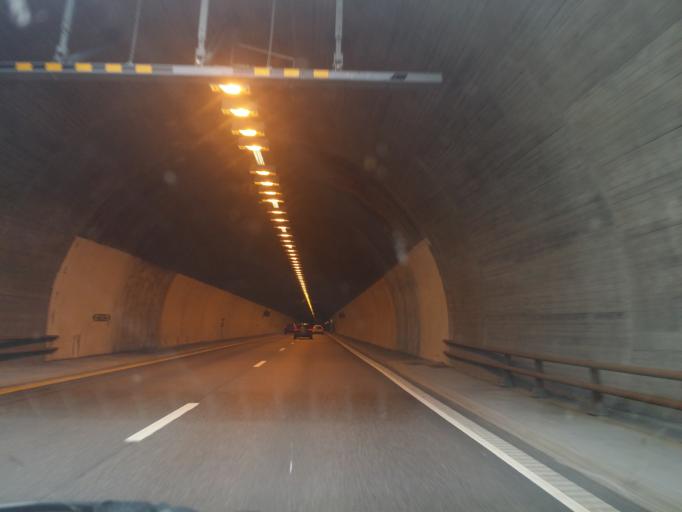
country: NO
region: Akershus
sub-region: Eidsvoll
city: Raholt
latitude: 60.3371
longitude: 11.1968
